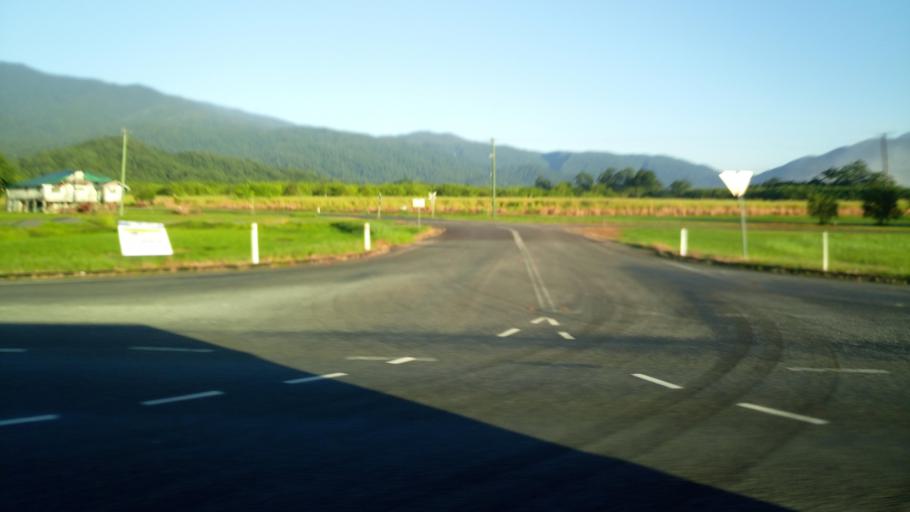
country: AU
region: Queensland
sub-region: Cassowary Coast
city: Innisfail
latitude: -17.3692
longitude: 145.9141
